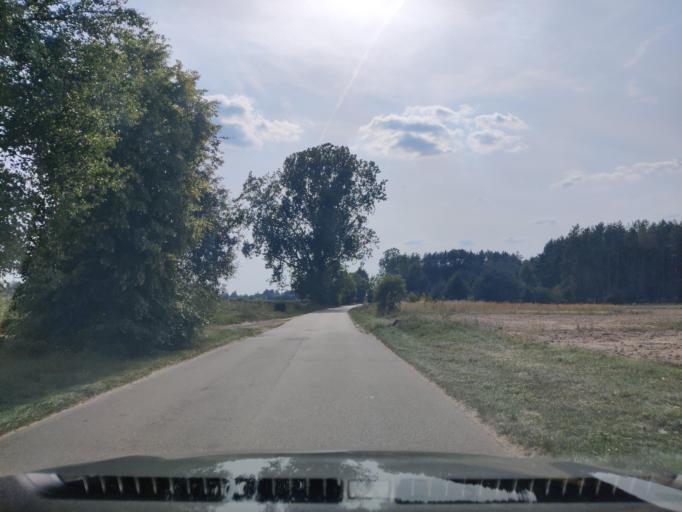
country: PL
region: Masovian Voivodeship
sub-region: Powiat wyszkowski
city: Rzasnik
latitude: 52.7683
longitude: 21.4003
